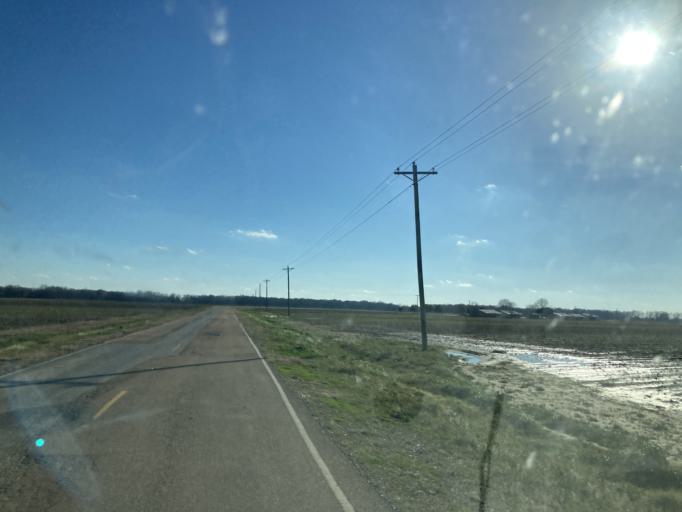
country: US
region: Mississippi
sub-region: Yazoo County
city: Yazoo City
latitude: 32.9278
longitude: -90.5058
